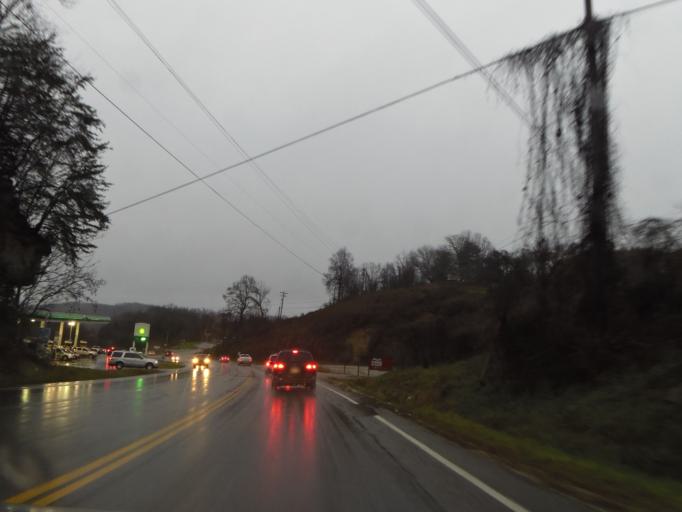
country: US
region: Kentucky
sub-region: Rockcastle County
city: Mount Vernon
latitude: 37.3446
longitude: -84.3150
